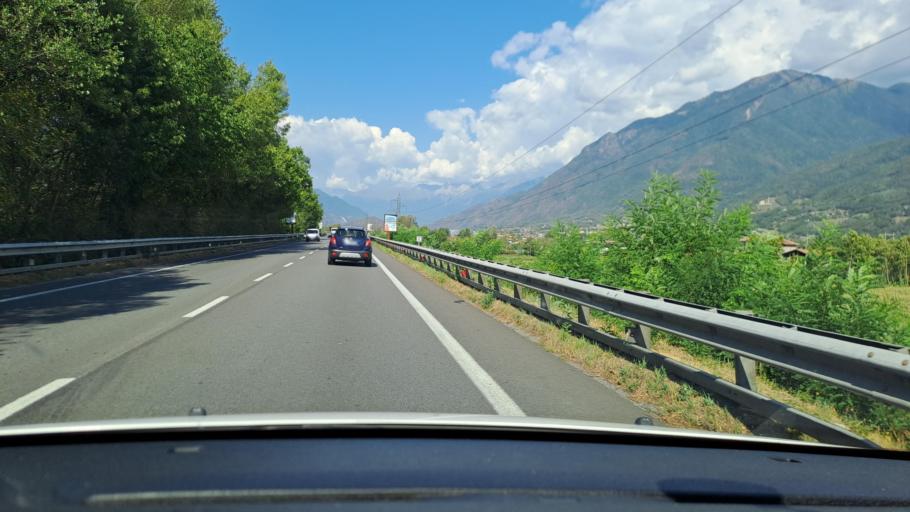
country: IT
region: Lombardy
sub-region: Provincia di Brescia
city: Pian Camuno
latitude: 45.8544
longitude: 10.1464
